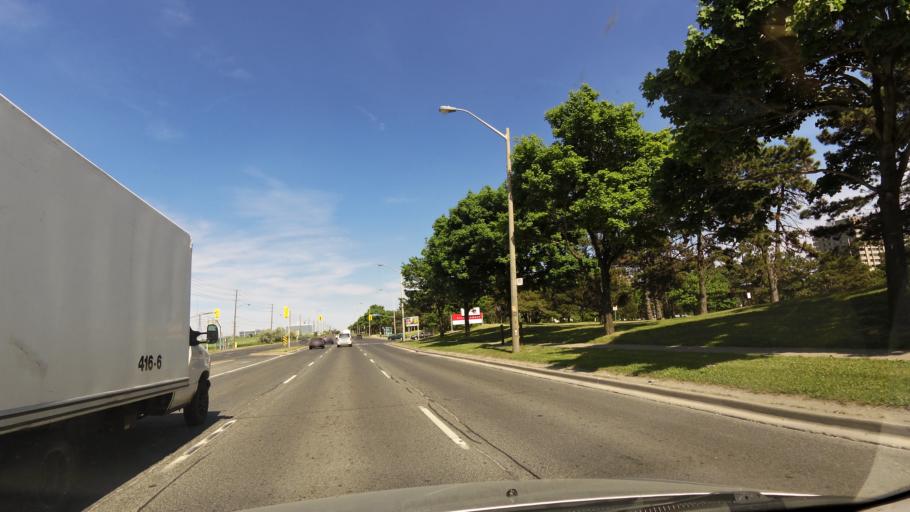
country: CA
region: Ontario
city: Concord
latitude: 43.7789
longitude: -79.5055
